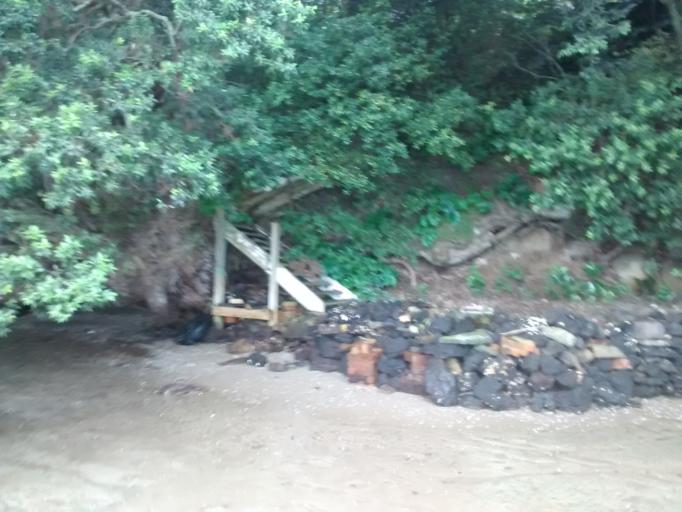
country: NZ
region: Auckland
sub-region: Auckland
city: Rosebank
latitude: -36.8531
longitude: 174.7135
